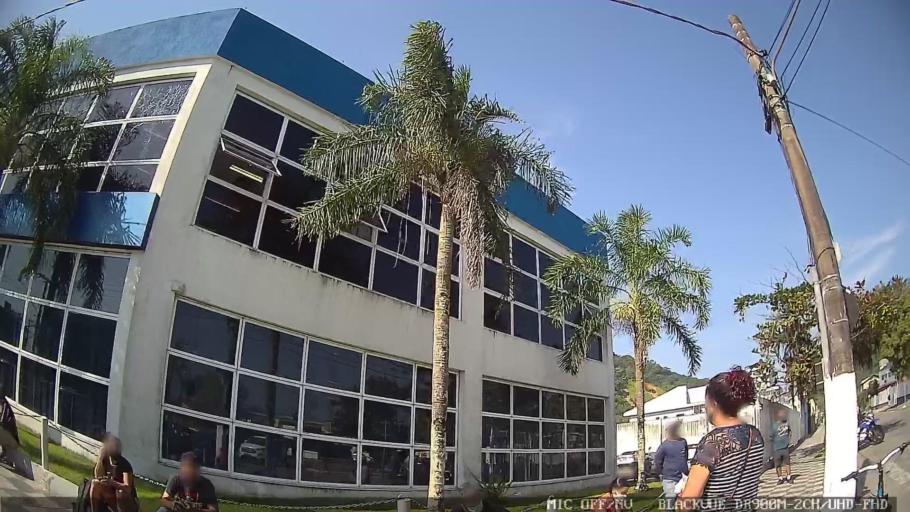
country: BR
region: Sao Paulo
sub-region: Guaruja
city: Guaruja
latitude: -23.9925
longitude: -46.2725
